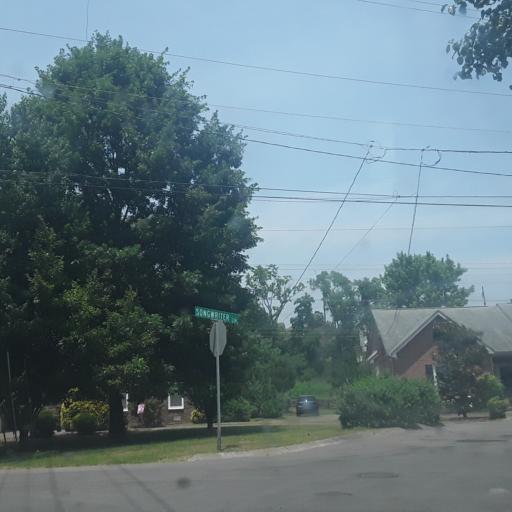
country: US
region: Tennessee
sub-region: Williamson County
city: Brentwood
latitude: 36.0519
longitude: -86.7518
